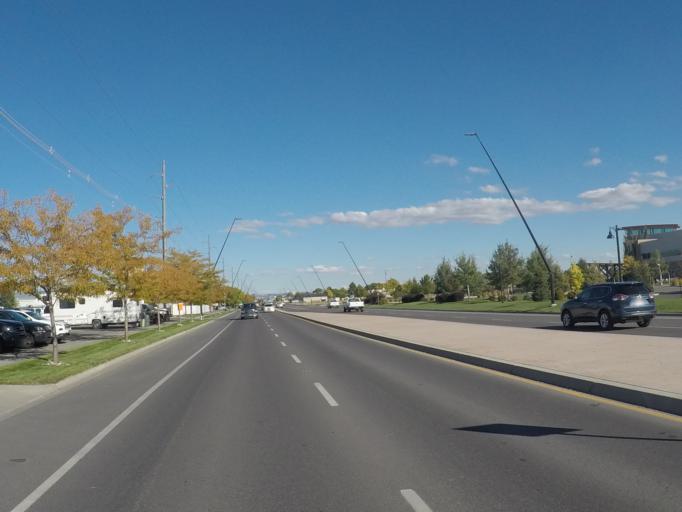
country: US
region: Montana
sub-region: Yellowstone County
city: Billings
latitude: 45.7842
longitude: -108.5980
